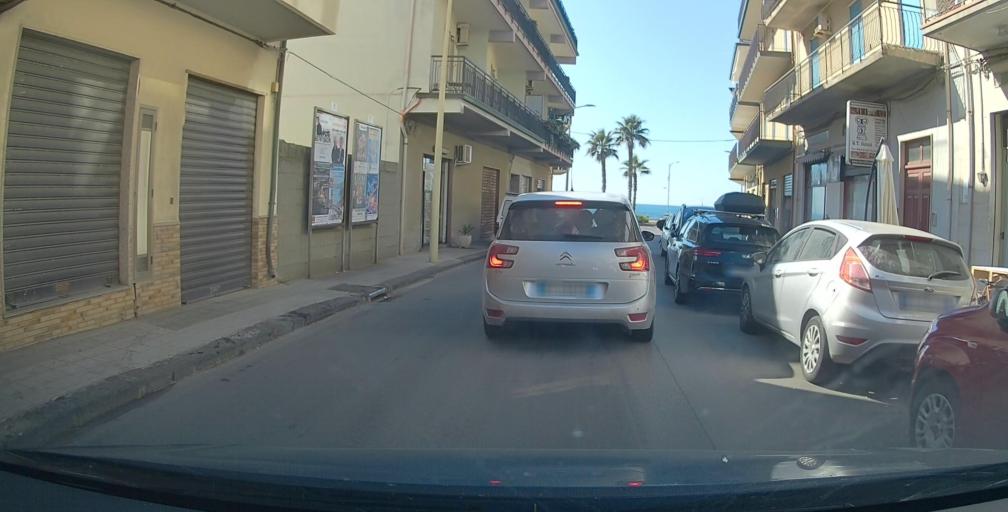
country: IT
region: Sicily
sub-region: Messina
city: Capo d'Orlando
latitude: 38.1636
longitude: 14.7473
